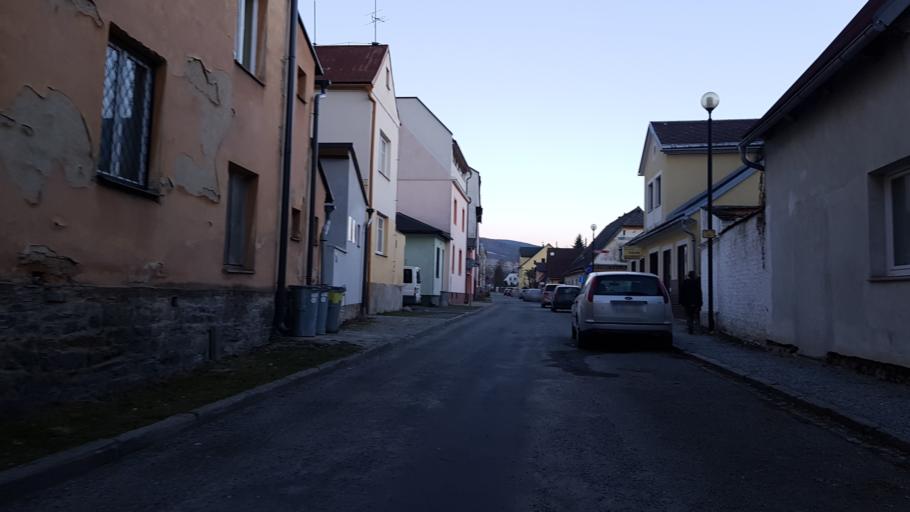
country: CZ
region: Olomoucky
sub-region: Okres Jesenik
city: Jesenik
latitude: 50.2261
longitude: 17.2058
